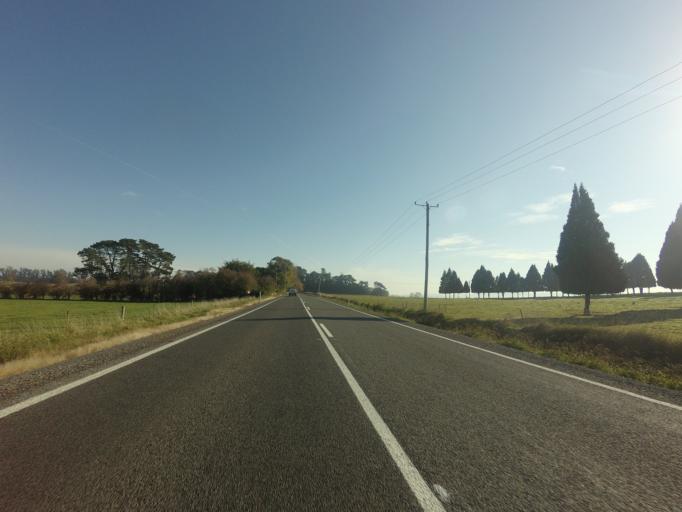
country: AU
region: Tasmania
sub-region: Northern Midlands
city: Longford
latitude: -41.5760
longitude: 147.1017
